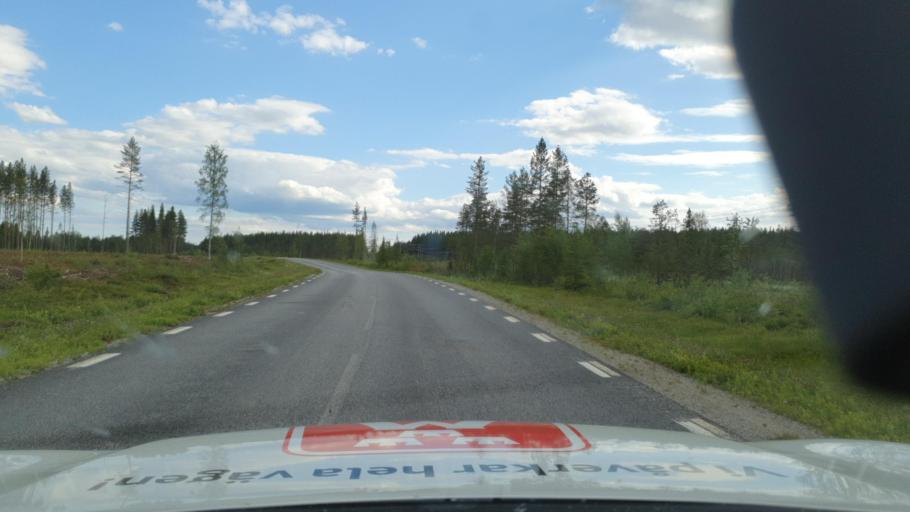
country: SE
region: Vaesterbotten
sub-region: Skelleftea Kommun
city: Langsele
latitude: 64.6028
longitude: 19.9319
